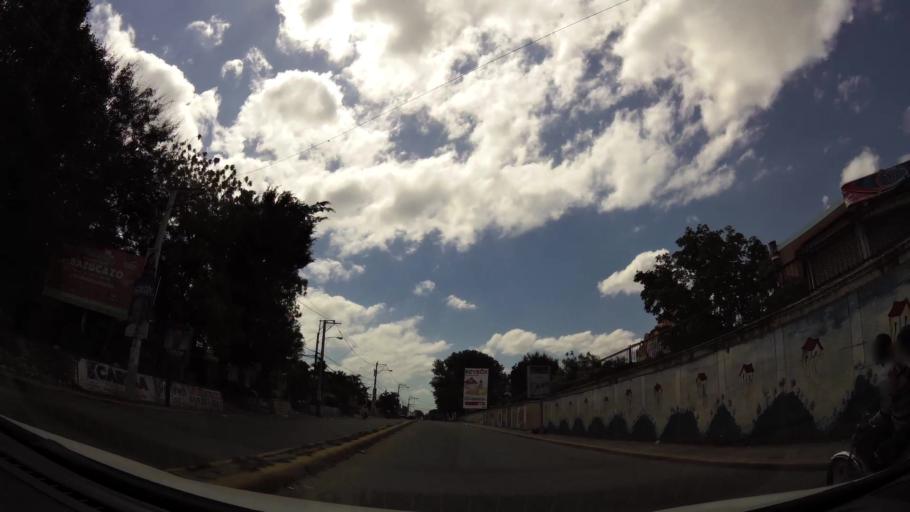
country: DO
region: San Cristobal
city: San Cristobal
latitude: 18.4239
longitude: -70.1161
